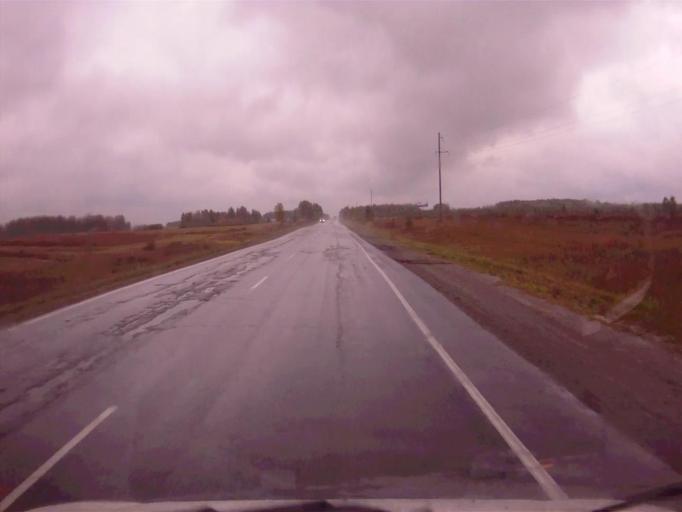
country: RU
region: Chelyabinsk
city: Novogornyy
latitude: 55.4883
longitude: 60.7051
